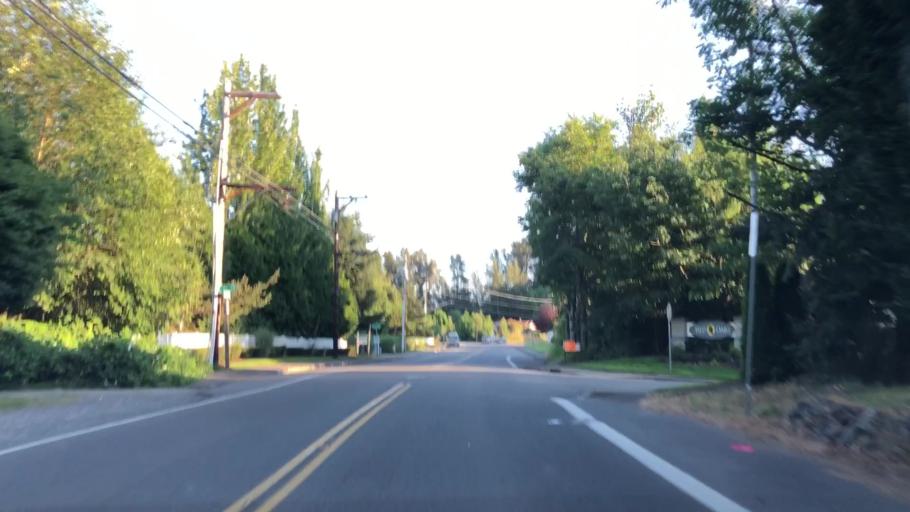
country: US
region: Washington
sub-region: Snohomish County
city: Martha Lake
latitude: 47.8612
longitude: -122.2690
